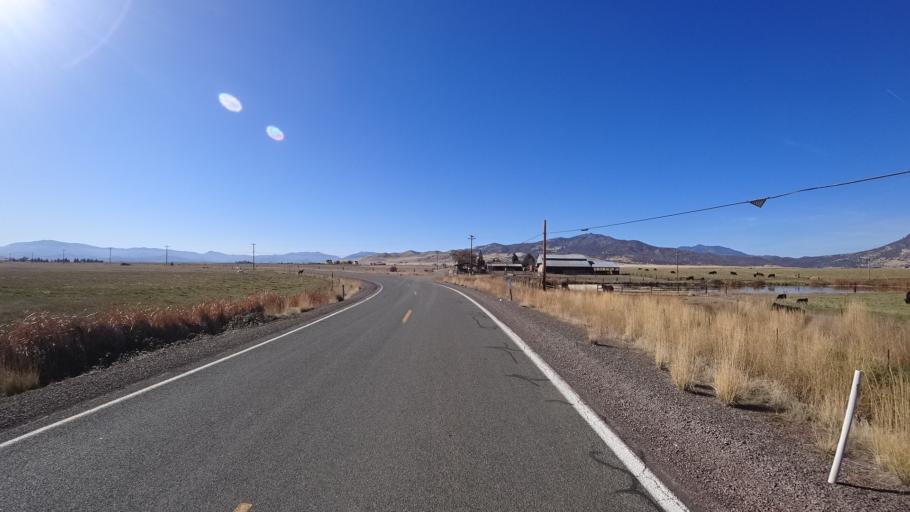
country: US
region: California
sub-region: Siskiyou County
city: Montague
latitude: 41.7938
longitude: -122.4685
